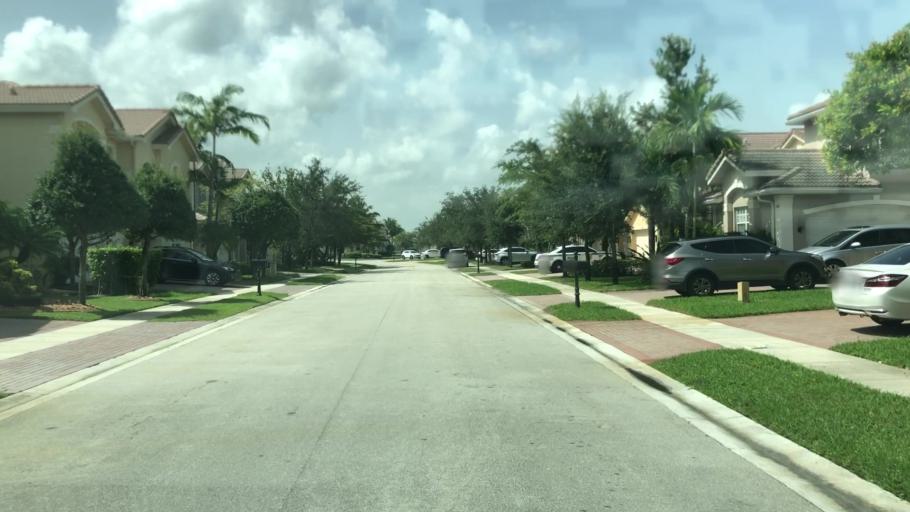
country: US
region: Florida
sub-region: Miami-Dade County
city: Palm Springs North
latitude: 25.9669
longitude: -80.3838
